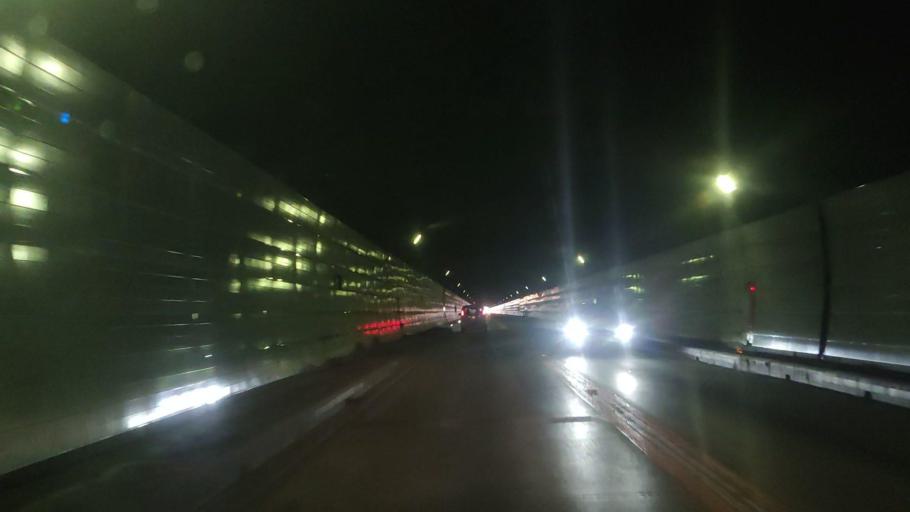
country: JP
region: Kumamoto
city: Hitoyoshi
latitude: 32.0957
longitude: 130.8030
